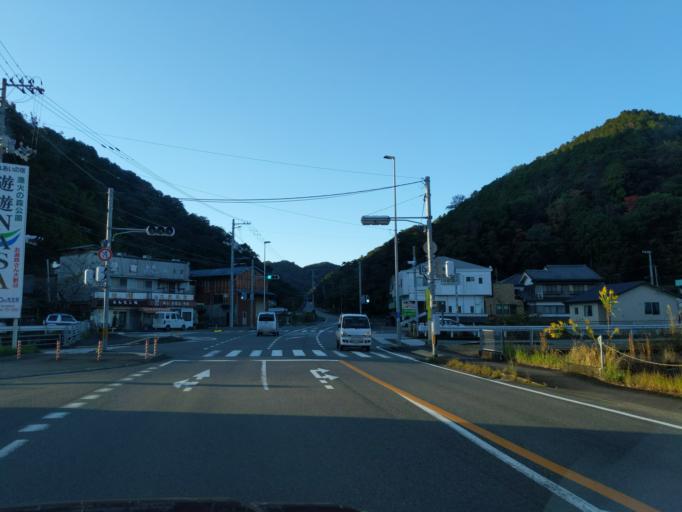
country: JP
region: Kochi
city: Muroto-misakicho
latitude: 33.5938
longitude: 134.3530
